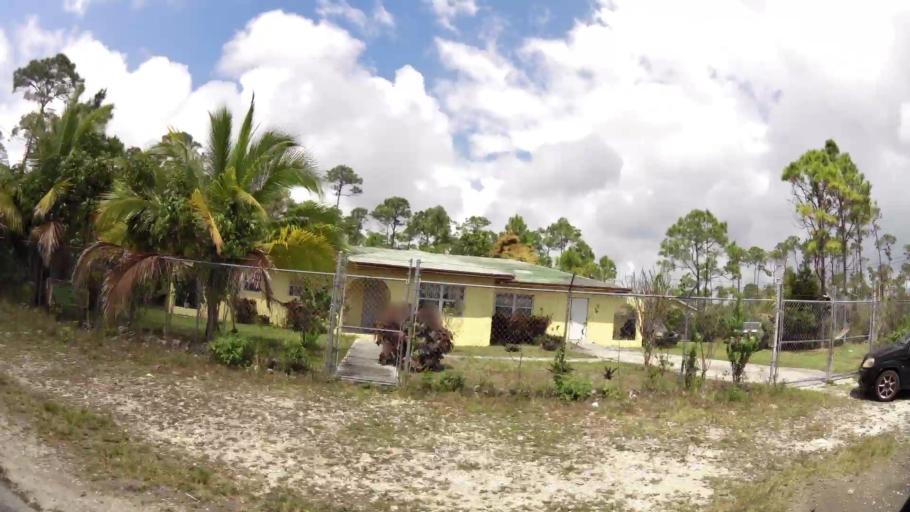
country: BS
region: Freeport
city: Lucaya
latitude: 26.5347
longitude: -78.6481
